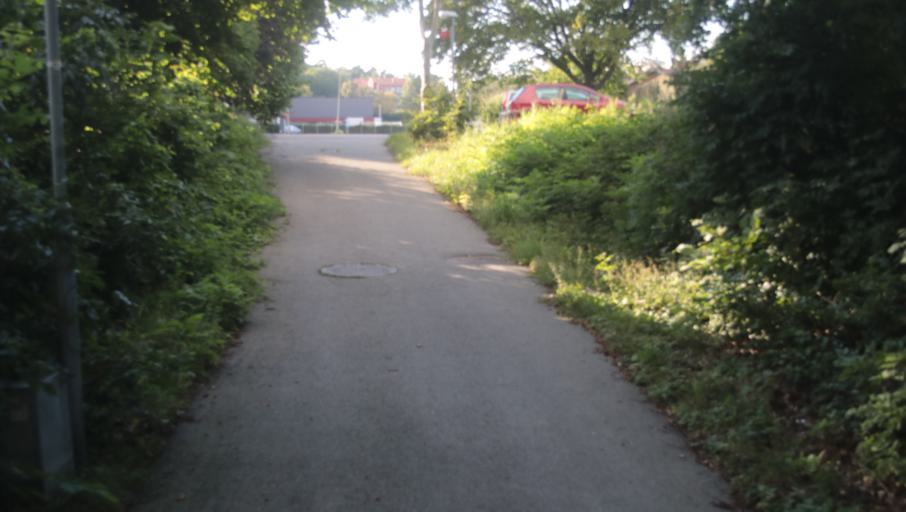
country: SE
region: Blekinge
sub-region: Karlshamns Kommun
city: Karlshamn
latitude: 56.1618
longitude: 14.8842
